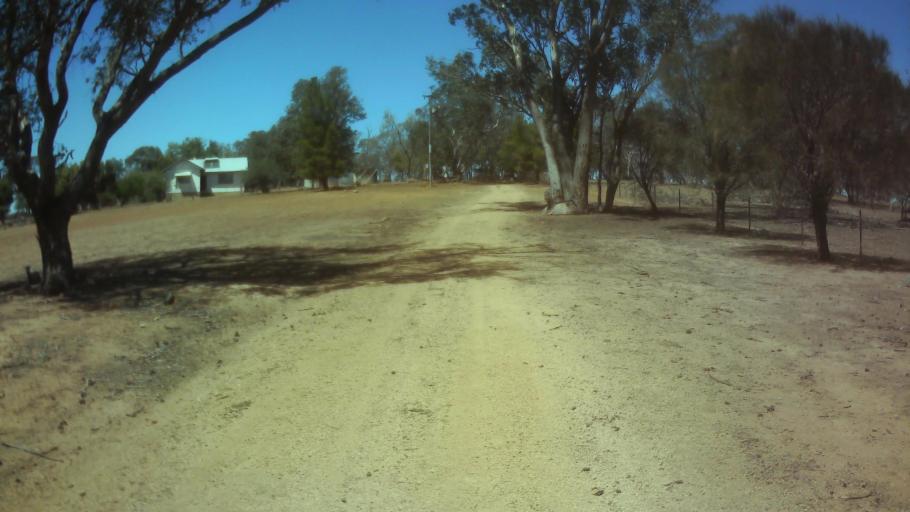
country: AU
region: New South Wales
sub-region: Cowra
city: Cowra
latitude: -33.9091
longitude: 148.5060
